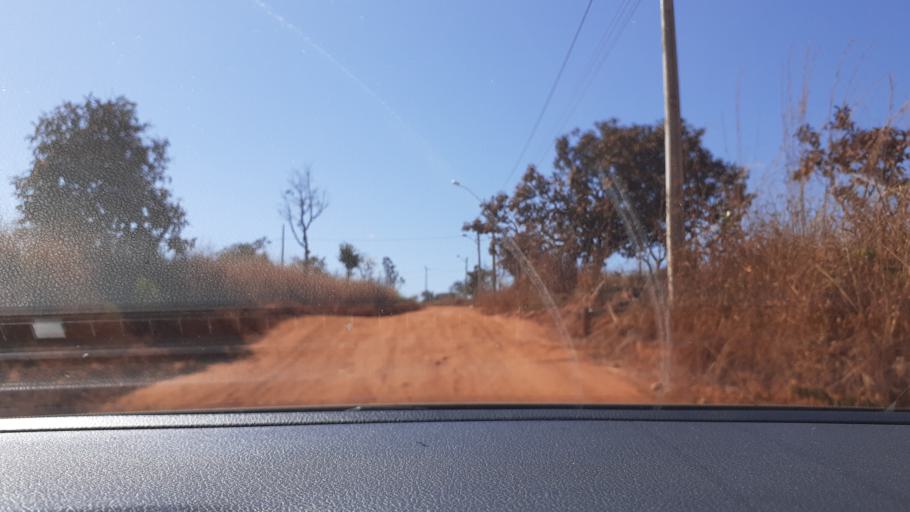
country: BR
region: Goias
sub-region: Aparecida De Goiania
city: Aparecida de Goiania
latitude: -16.8898
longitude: -49.2613
